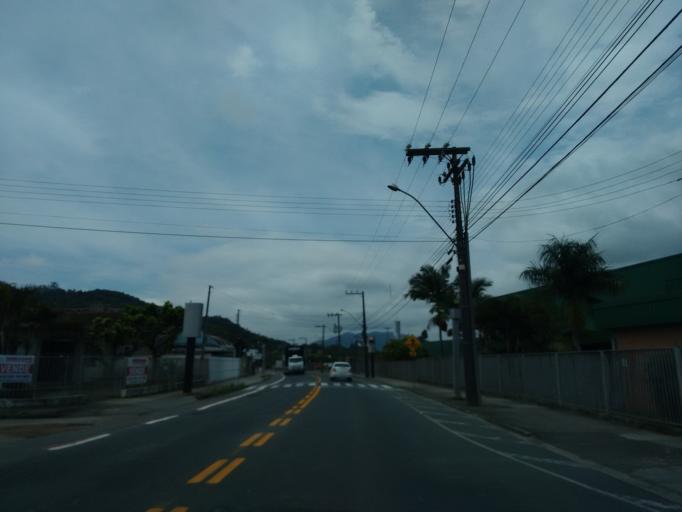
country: BR
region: Santa Catarina
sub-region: Pomerode
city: Pomerode
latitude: -26.7174
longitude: -49.1674
